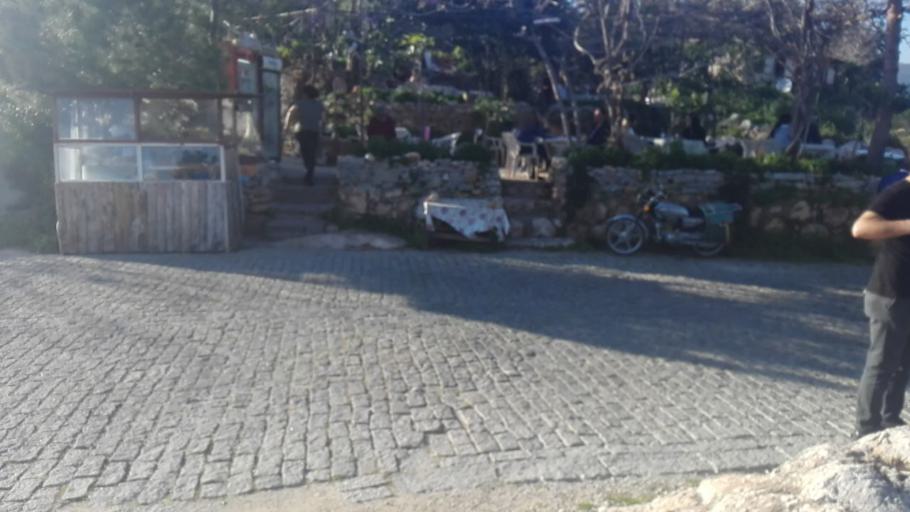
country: TR
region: Antalya
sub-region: Alanya
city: Alanya
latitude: 36.5318
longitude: 31.9929
